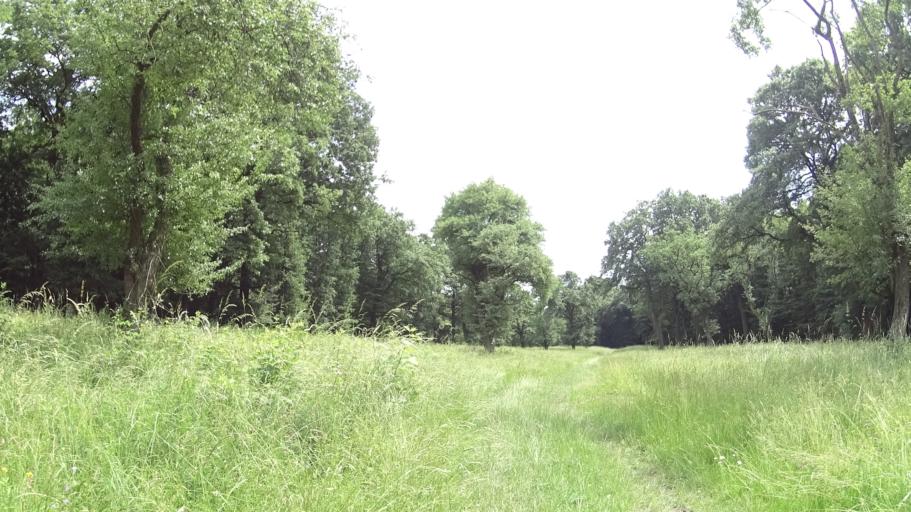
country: HU
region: Pest
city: Nagymaros
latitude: 47.8091
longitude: 18.9401
